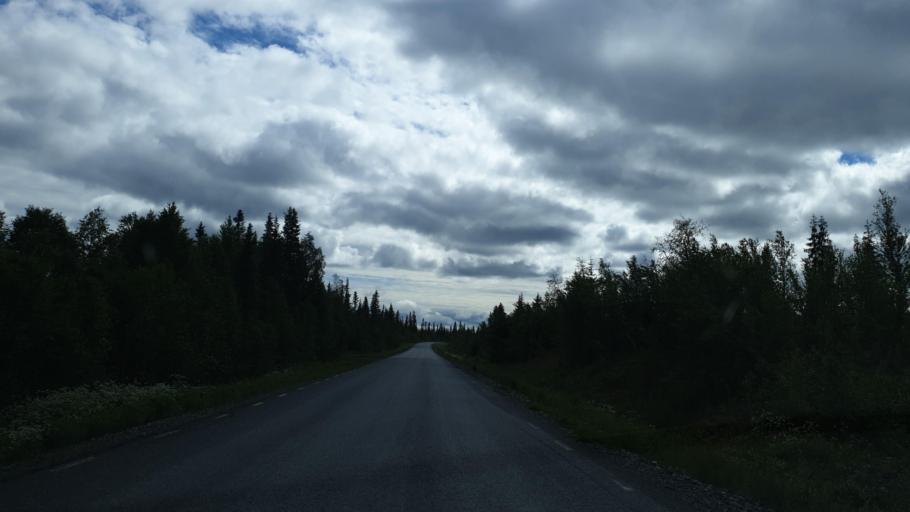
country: SE
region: Vaesterbotten
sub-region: Vilhelmina Kommun
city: Sjoberg
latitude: 65.1475
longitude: 15.8664
